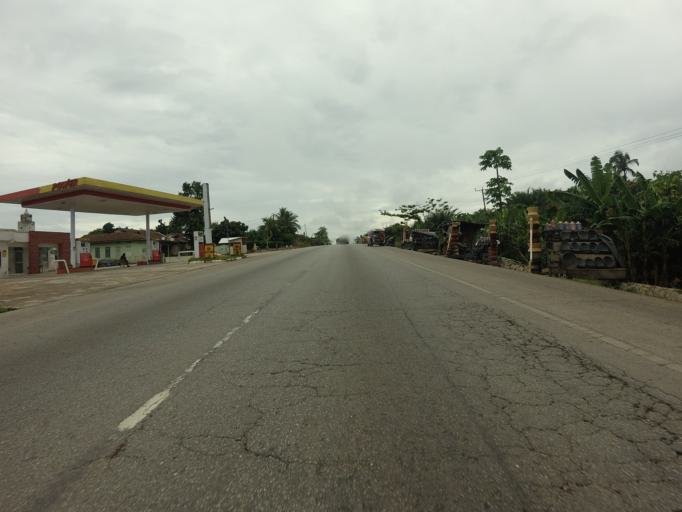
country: GH
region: Eastern
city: Nkawkaw
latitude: 6.4489
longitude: -0.6099
